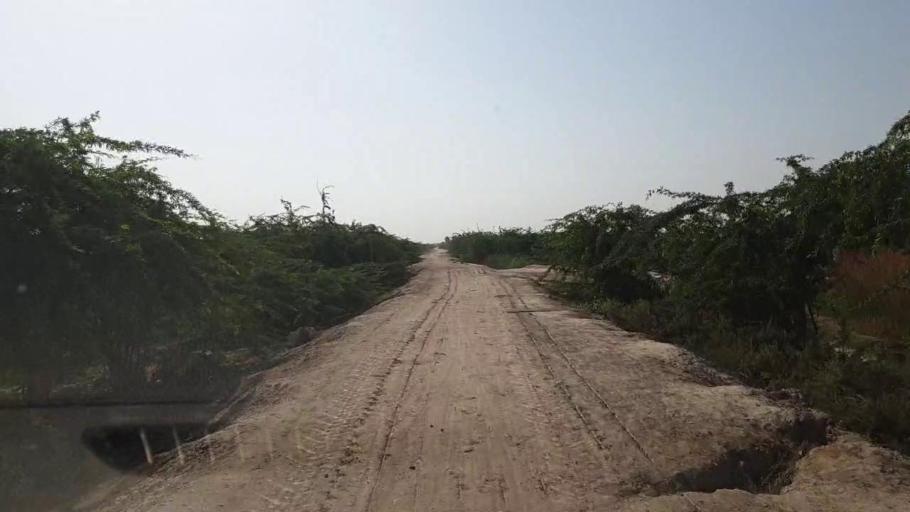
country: PK
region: Sindh
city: Kadhan
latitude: 24.5763
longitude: 69.0810
